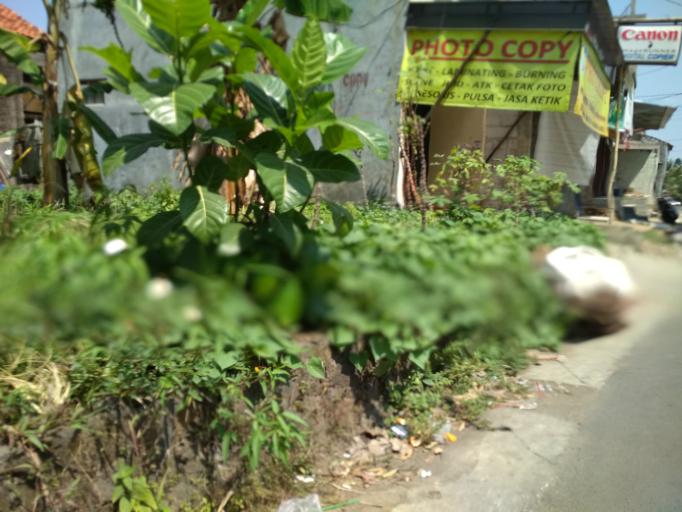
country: ID
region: West Java
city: Ciampea
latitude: -6.5555
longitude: 106.7478
